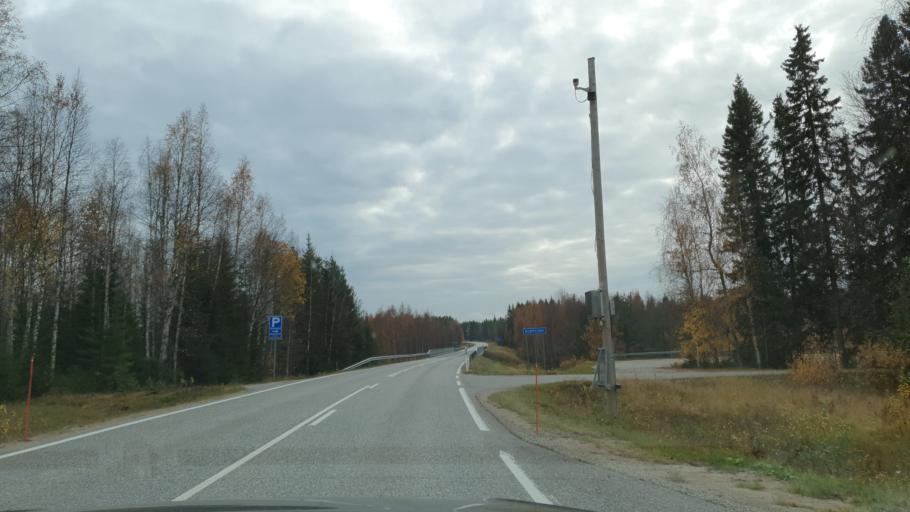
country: FI
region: Kainuu
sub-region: Kehys-Kainuu
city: Puolanka
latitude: 65.2476
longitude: 27.5787
